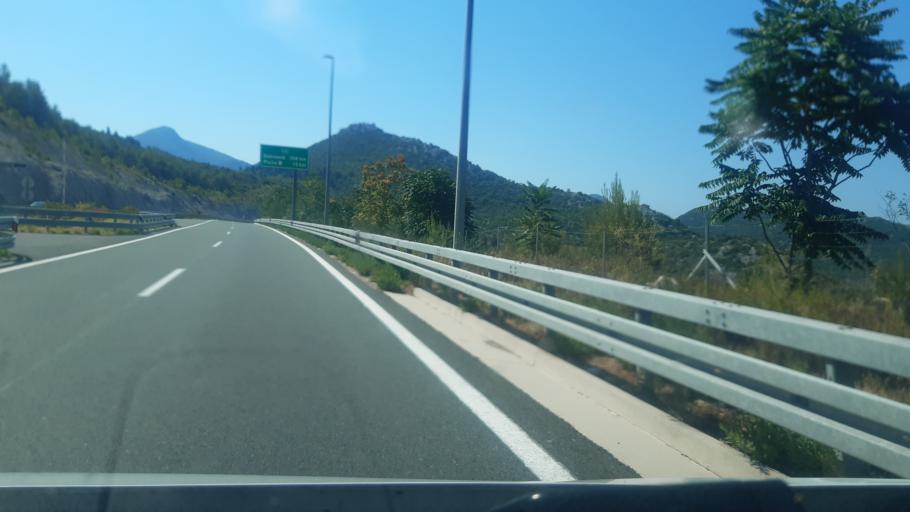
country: BA
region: Federation of Bosnia and Herzegovina
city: Ljubuski
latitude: 43.1349
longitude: 17.4831
